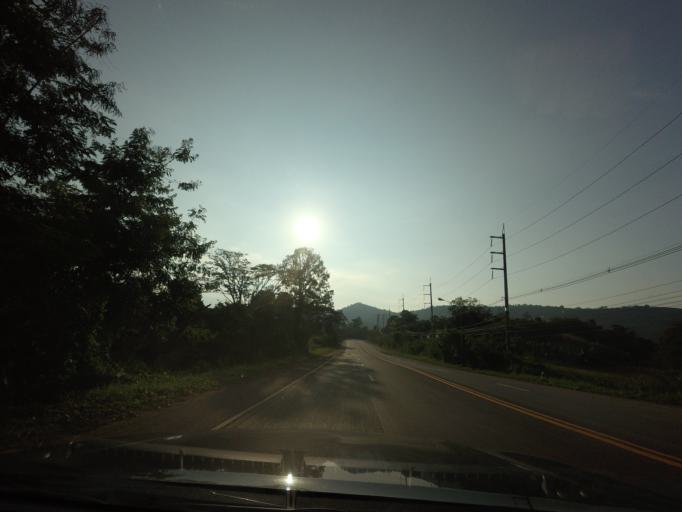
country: TH
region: Loei
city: Dan Sai
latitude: 17.2104
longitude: 101.1563
